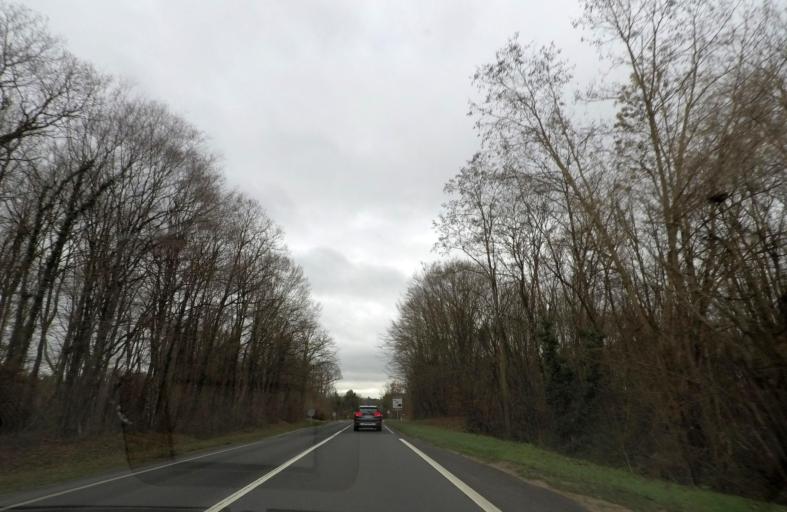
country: FR
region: Centre
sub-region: Departement du Loir-et-Cher
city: Cellettes
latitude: 47.5357
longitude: 1.4135
